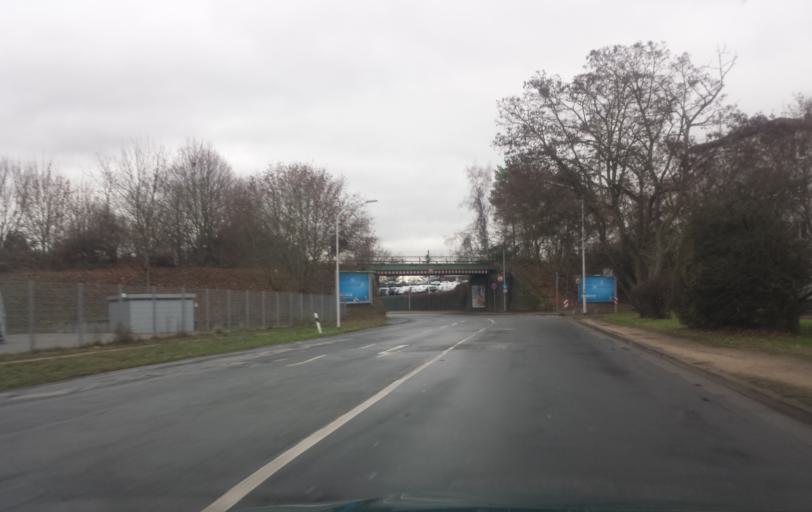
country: DE
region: Hesse
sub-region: Regierungsbezirk Darmstadt
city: Darmstadt
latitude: 49.8860
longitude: 8.6235
